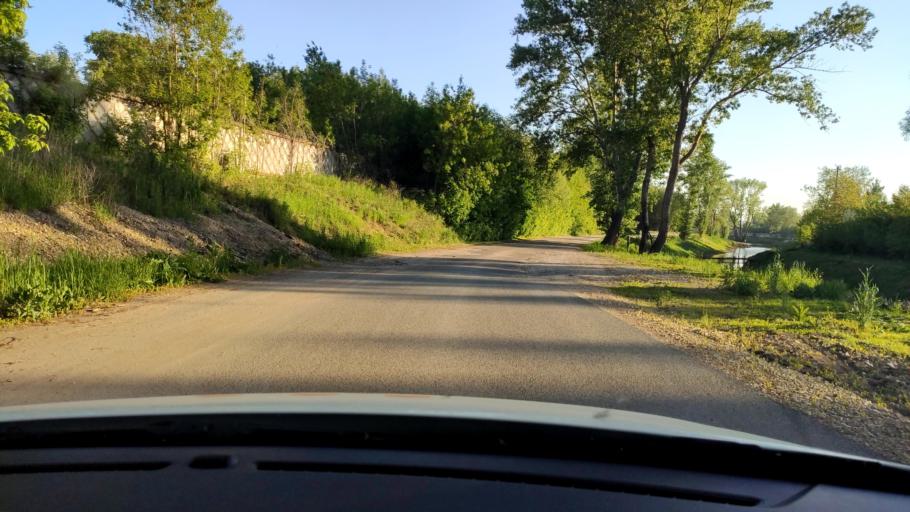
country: RU
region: Tatarstan
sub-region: Gorod Kazan'
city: Kazan
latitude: 55.8031
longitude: 49.0510
